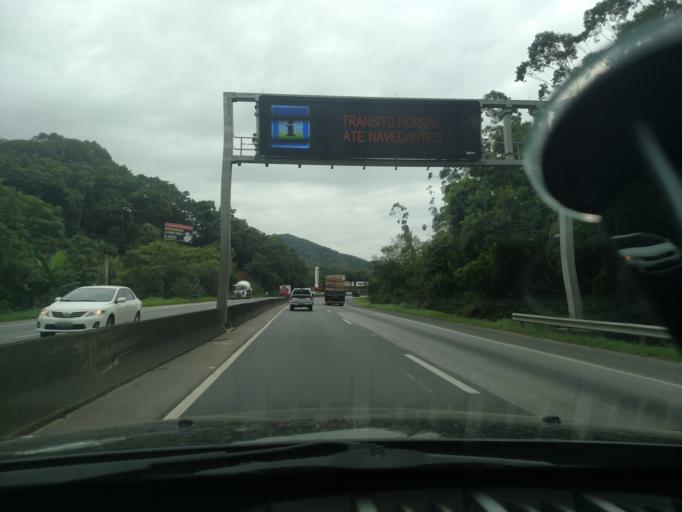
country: BR
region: Santa Catarina
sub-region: Balneario Camboriu
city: Balneario Camboriu
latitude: -26.9684
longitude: -48.6836
